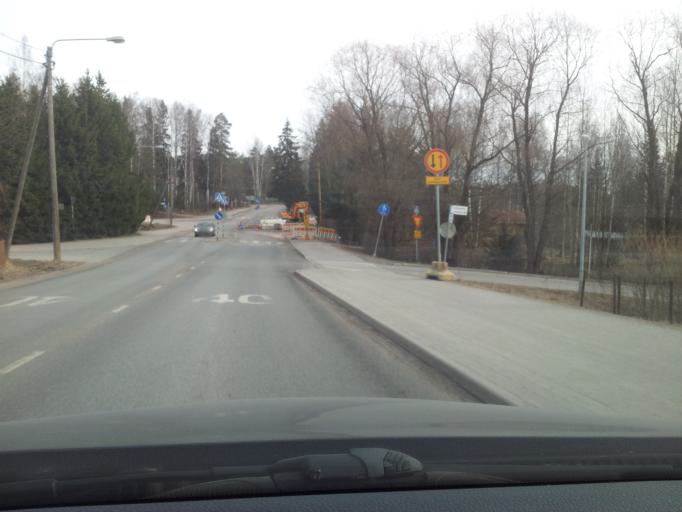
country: FI
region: Uusimaa
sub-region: Helsinki
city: Kilo
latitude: 60.1909
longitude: 24.7633
